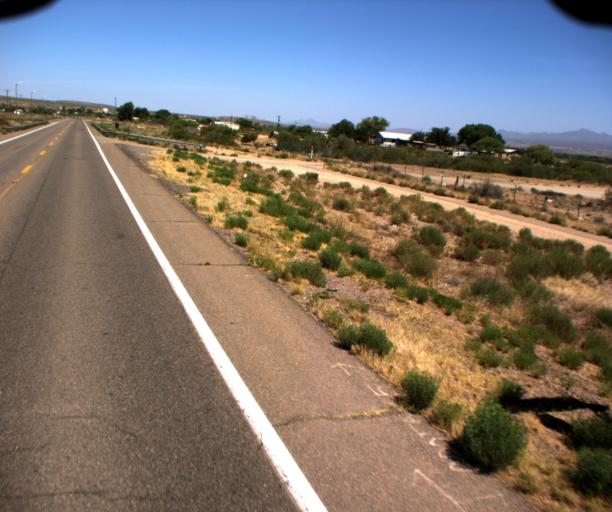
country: US
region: Arizona
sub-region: Graham County
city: Bylas
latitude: 33.1131
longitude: -110.0989
